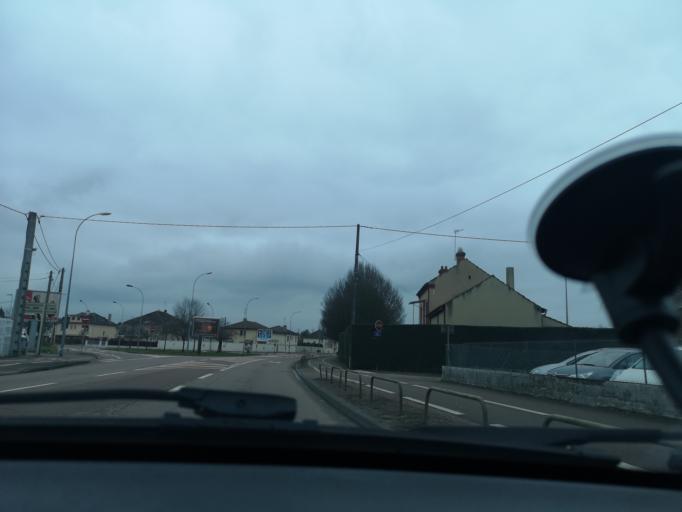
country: FR
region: Bourgogne
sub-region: Departement de Saone-et-Loire
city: Champforgeuil
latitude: 46.8090
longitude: 4.8520
